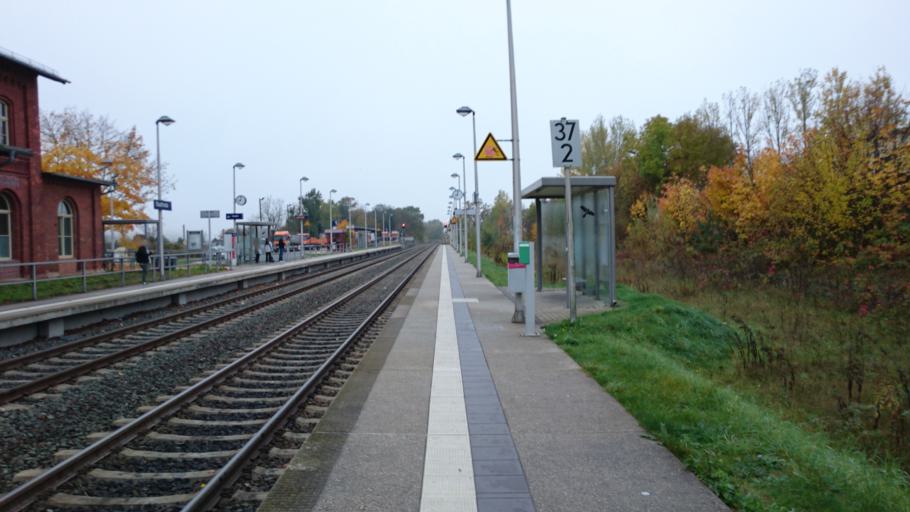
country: DE
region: Thuringia
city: Stadtroda
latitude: 50.8681
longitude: 11.7233
